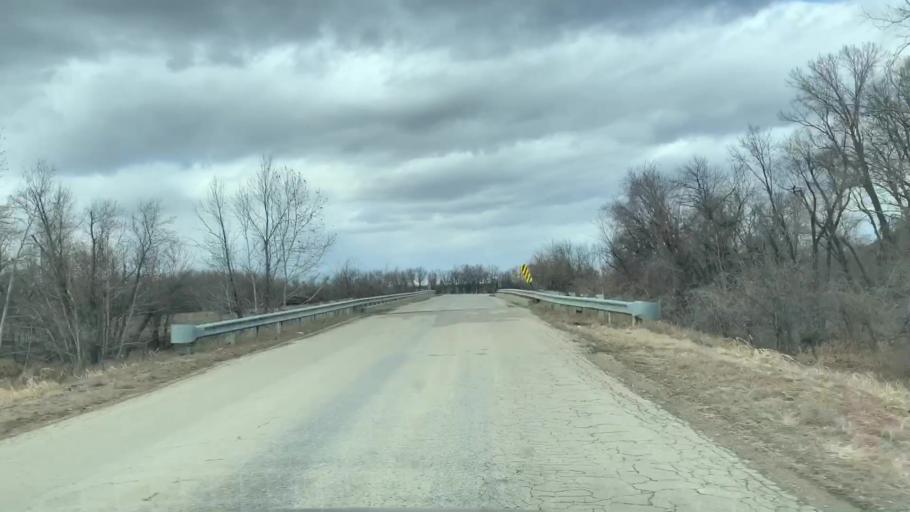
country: US
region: Kansas
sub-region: Allen County
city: Humboldt
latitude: 37.8038
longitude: -95.4712
